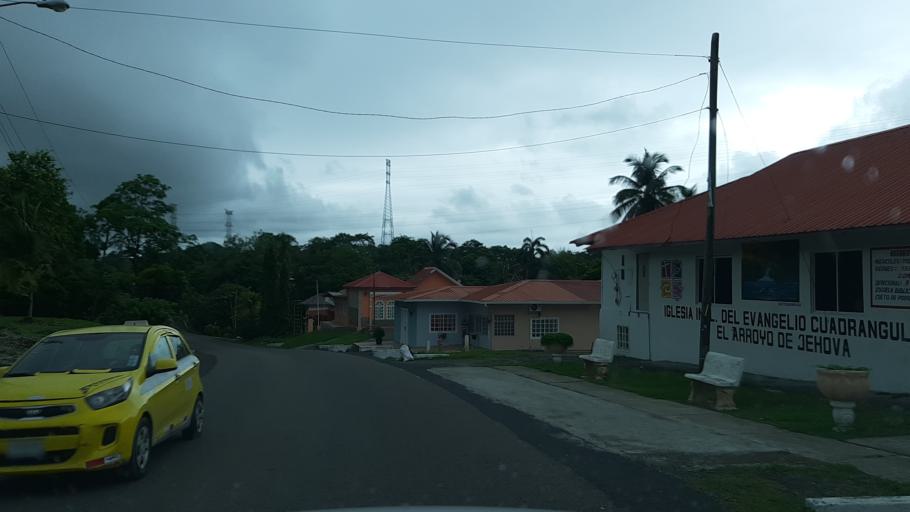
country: PA
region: Colon
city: Nuevo San Juan
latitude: 9.2397
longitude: -79.6591
